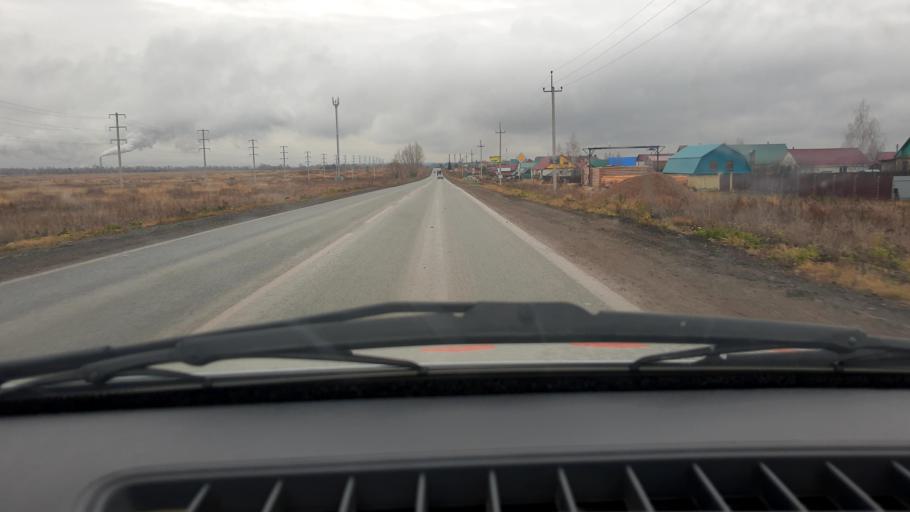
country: RU
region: Bashkortostan
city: Iglino
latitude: 54.7877
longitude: 56.2519
